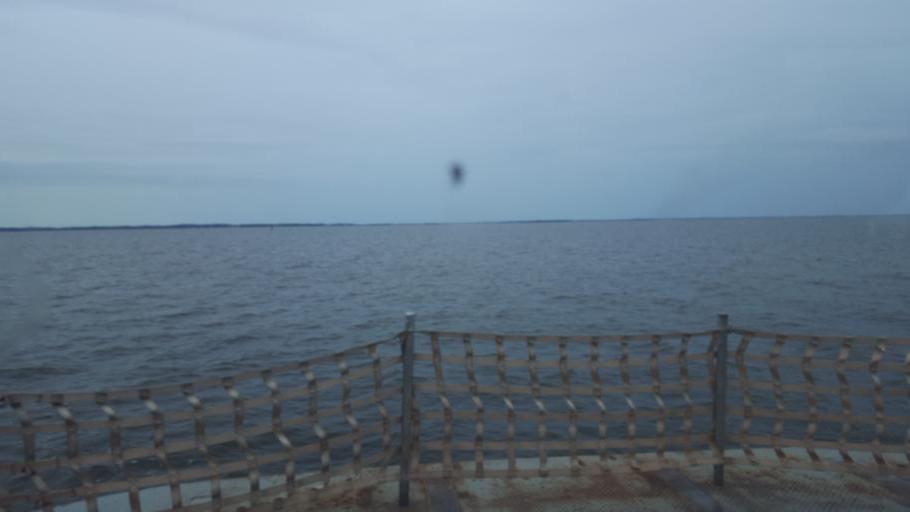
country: US
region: North Carolina
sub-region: Currituck County
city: Currituck
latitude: 36.4582
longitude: -75.9803
